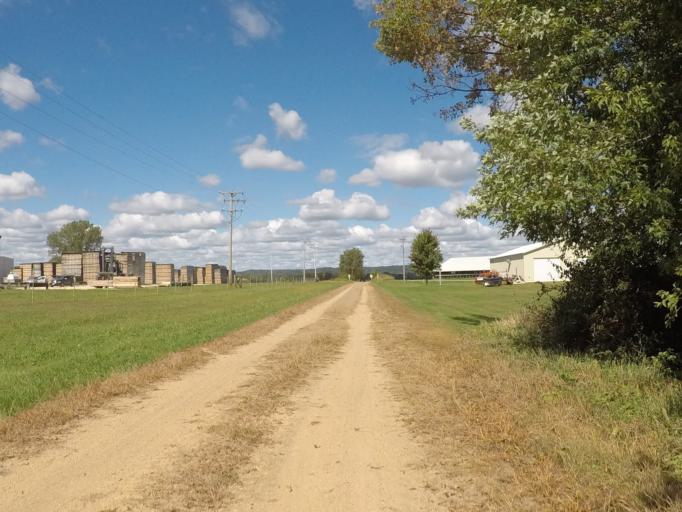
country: US
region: Wisconsin
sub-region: Richland County
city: Richland Center
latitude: 43.2919
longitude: -90.3264
